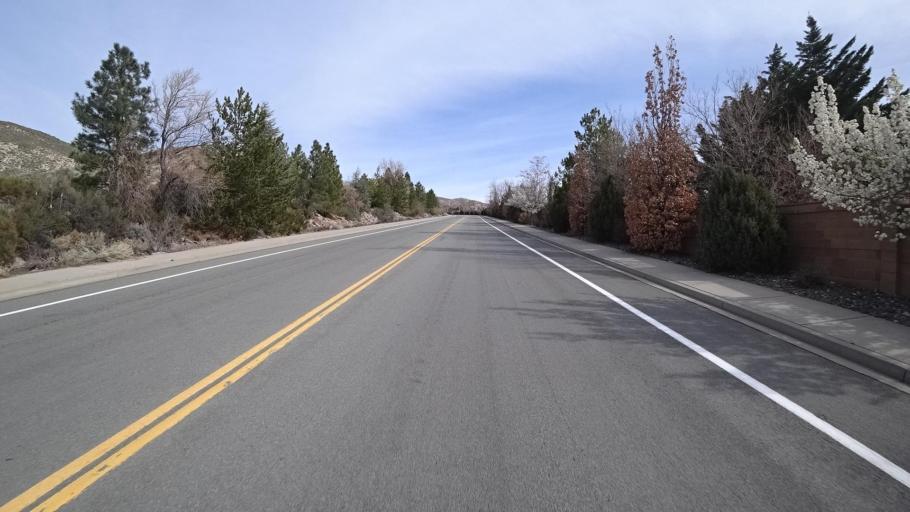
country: US
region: Nevada
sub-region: Washoe County
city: Mogul
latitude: 39.5352
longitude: -119.8959
